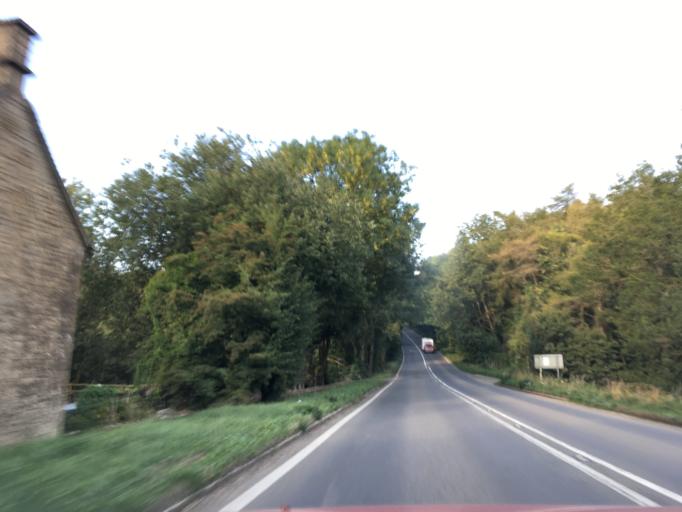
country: GB
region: England
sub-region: Gloucestershire
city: Bourton on the Water
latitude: 51.8670
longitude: -1.7953
